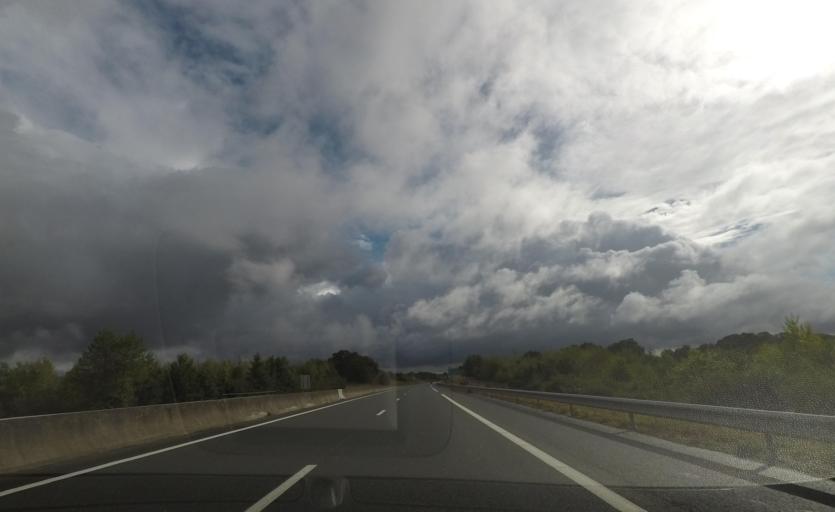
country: FR
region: Pays de la Loire
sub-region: Departement de la Vendee
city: La Roche-sur-Yon
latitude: 46.6628
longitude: -1.3700
